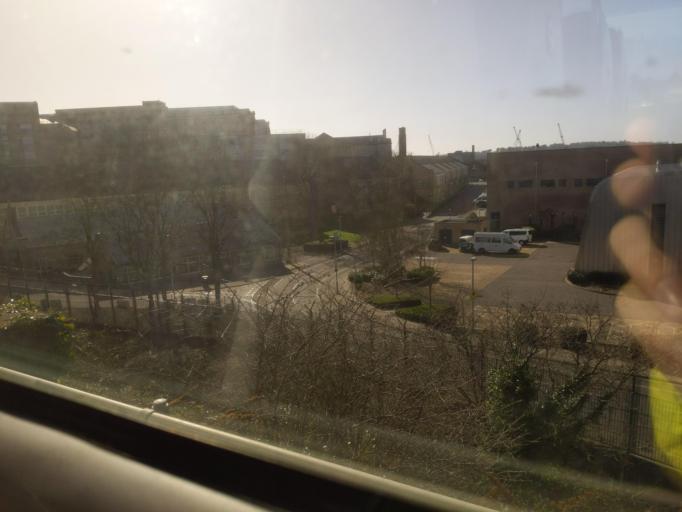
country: GB
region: England
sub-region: Cornwall
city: Torpoint
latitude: 50.3935
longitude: -4.1818
